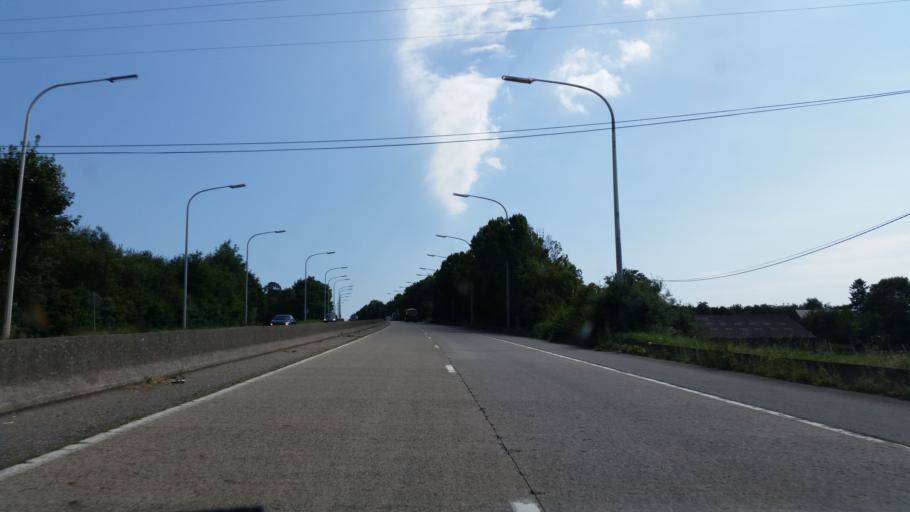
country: BE
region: Wallonia
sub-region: Province de Namur
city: Hamois
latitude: 50.3129
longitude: 5.1403
